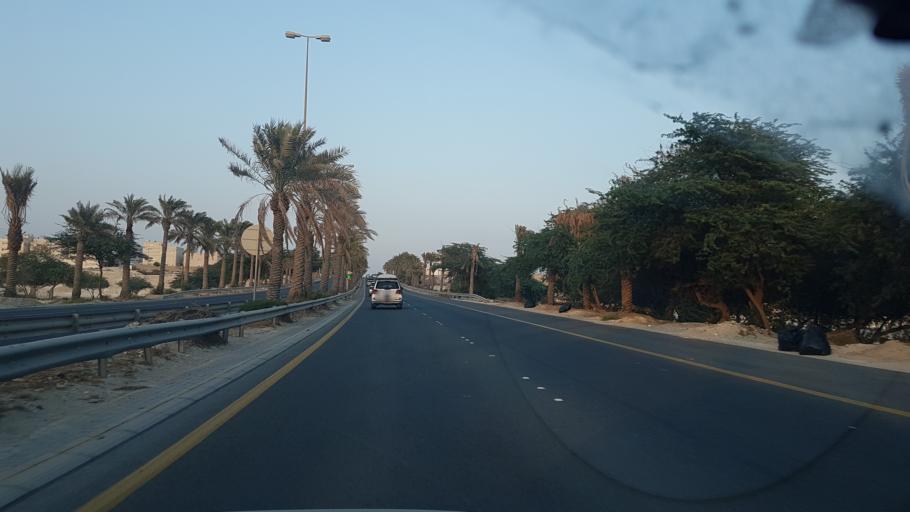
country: BH
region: Northern
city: Ar Rifa'
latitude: 26.1083
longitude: 50.5726
